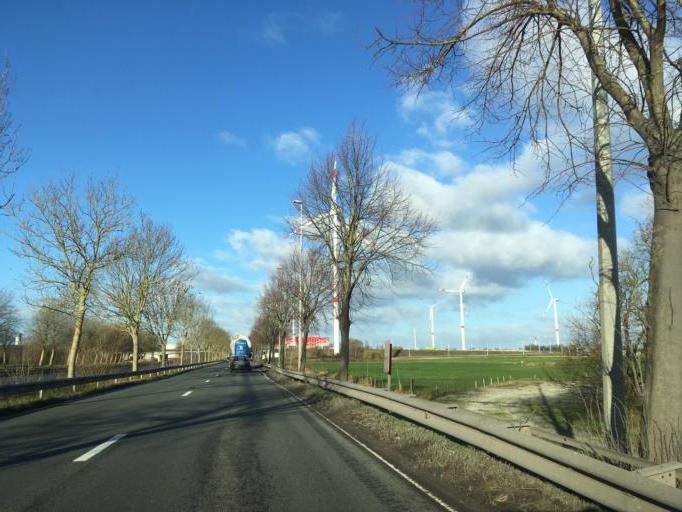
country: BE
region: Flanders
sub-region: Provincie West-Vlaanderen
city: Izegem
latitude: 50.9334
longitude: 3.1787
